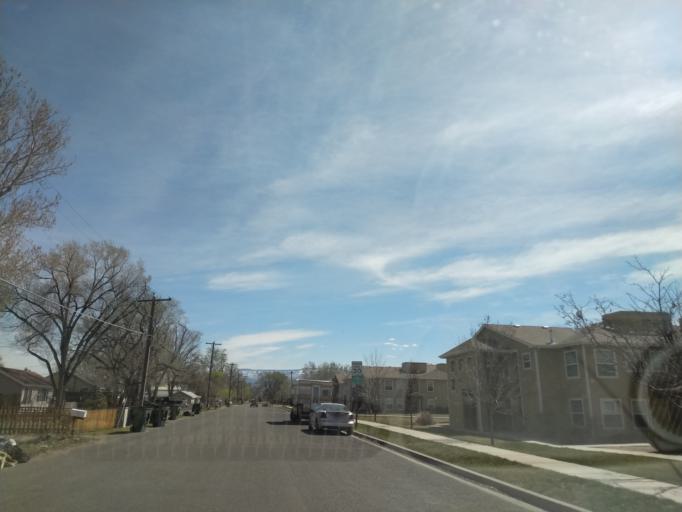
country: US
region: Colorado
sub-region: Mesa County
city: Grand Junction
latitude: 39.0810
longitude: -108.5326
